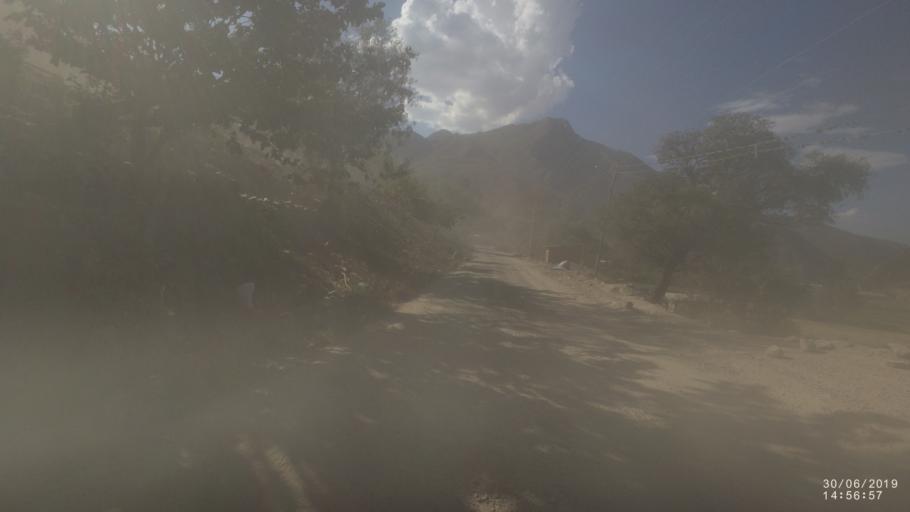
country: BO
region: Cochabamba
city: Irpa Irpa
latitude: -17.7463
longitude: -66.3541
